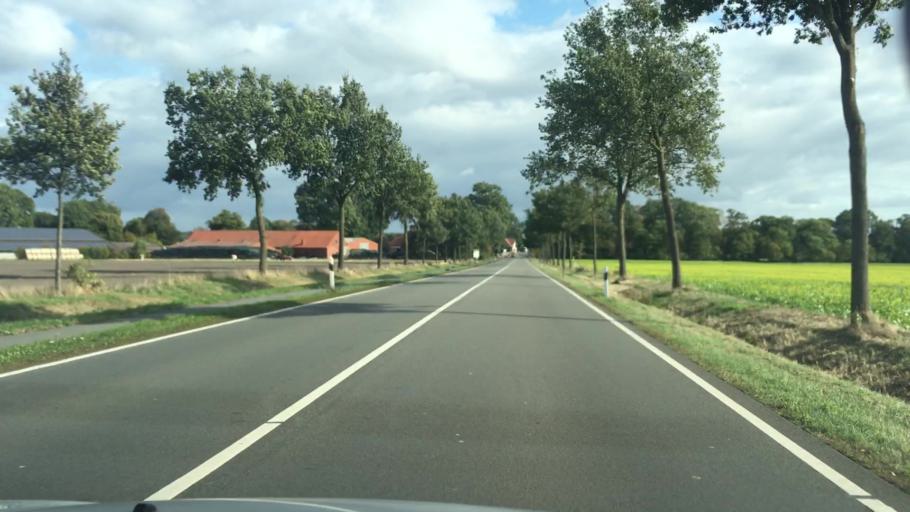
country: DE
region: Lower Saxony
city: Rehden
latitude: 52.6115
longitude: 8.4725
